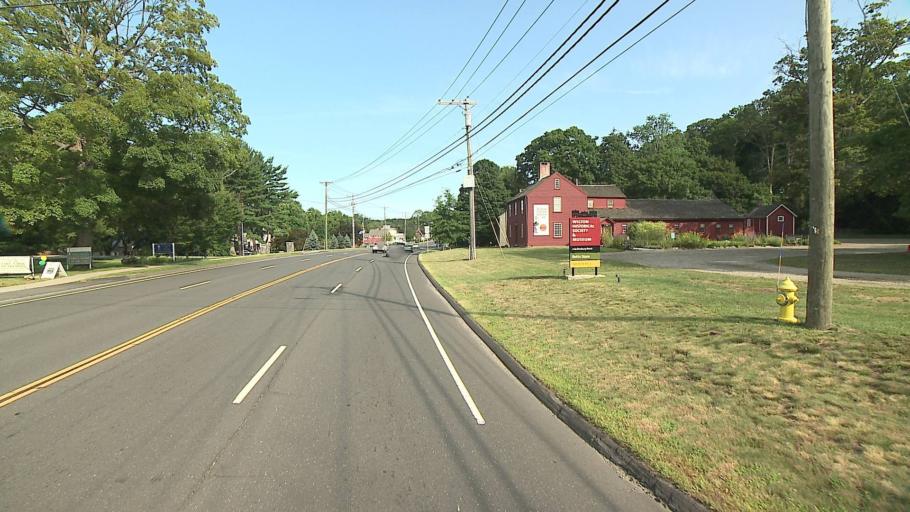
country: US
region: Connecticut
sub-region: Fairfield County
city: Wilton
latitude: 41.1877
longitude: -73.4246
